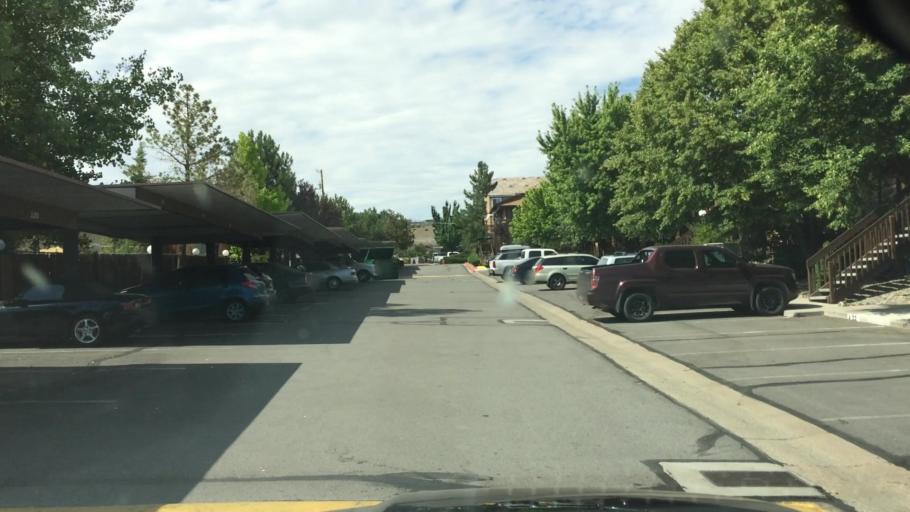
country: US
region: Nevada
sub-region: Washoe County
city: Reno
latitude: 39.5573
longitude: -119.7961
